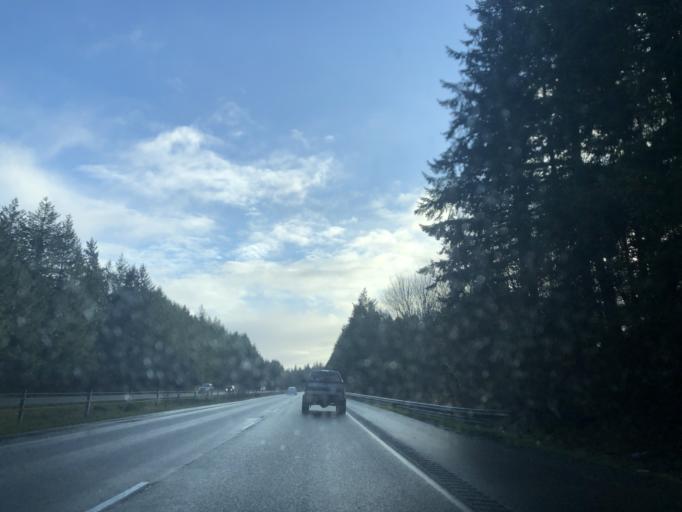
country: US
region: Washington
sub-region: Kitsap County
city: Erlands Point-Kitsap Lake
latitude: 47.5934
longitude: -122.6986
